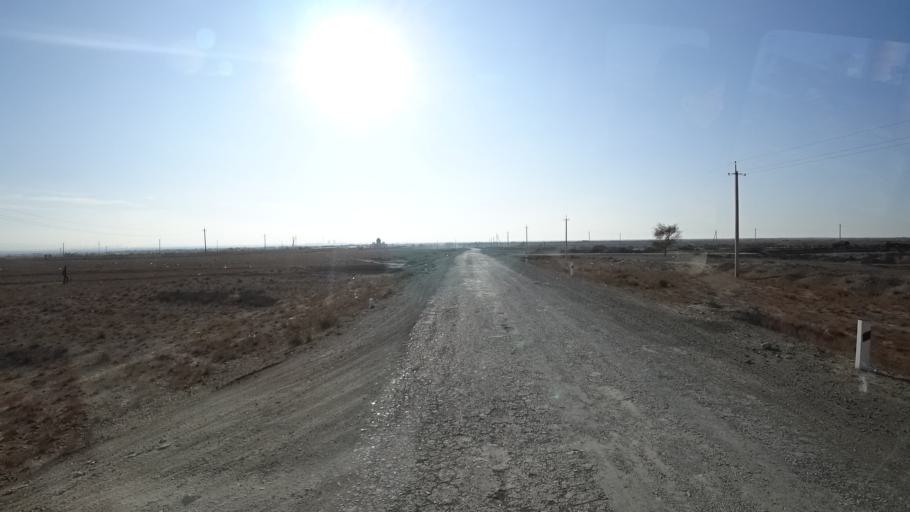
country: UZ
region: Navoiy
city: Beshrabot
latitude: 40.2224
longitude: 65.3914
